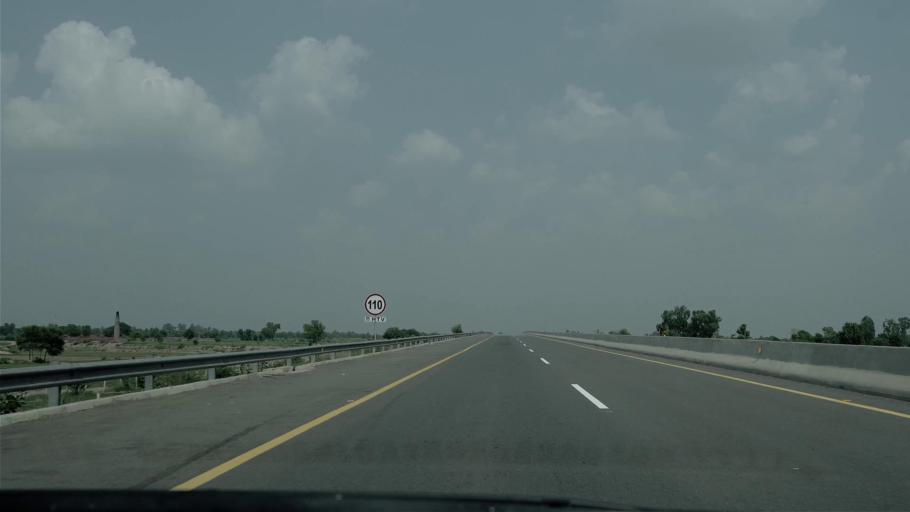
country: PK
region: Punjab
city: Gojra
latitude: 31.1946
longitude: 72.6532
